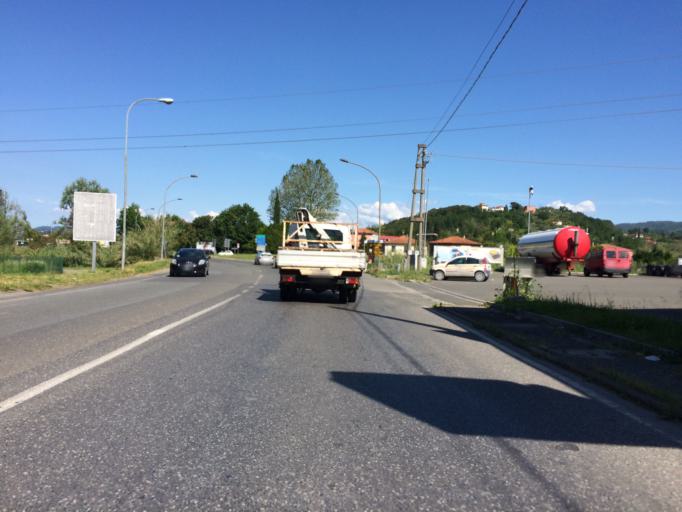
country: IT
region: Tuscany
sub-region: Provincia di Massa-Carrara
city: Borghetto-Melara
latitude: 44.1028
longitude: 9.9784
